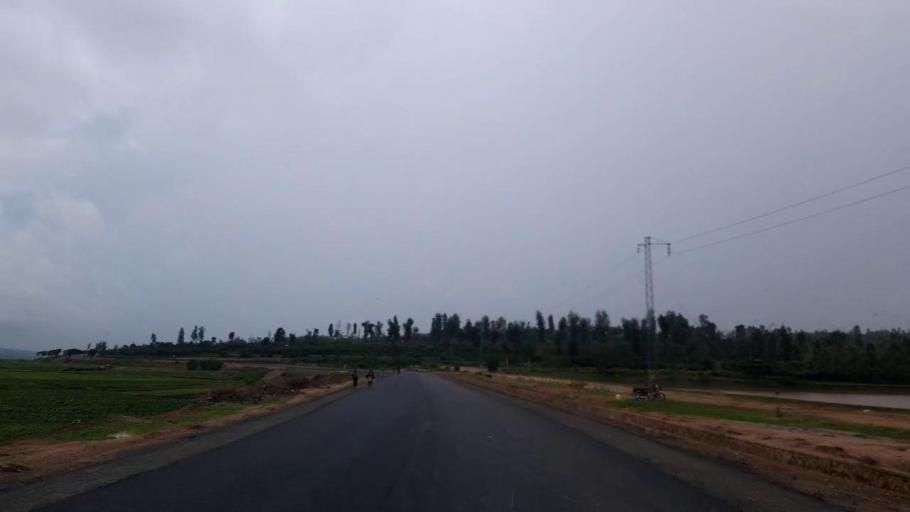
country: RW
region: Northern Province
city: Byumba
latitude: -1.4110
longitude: 30.2847
